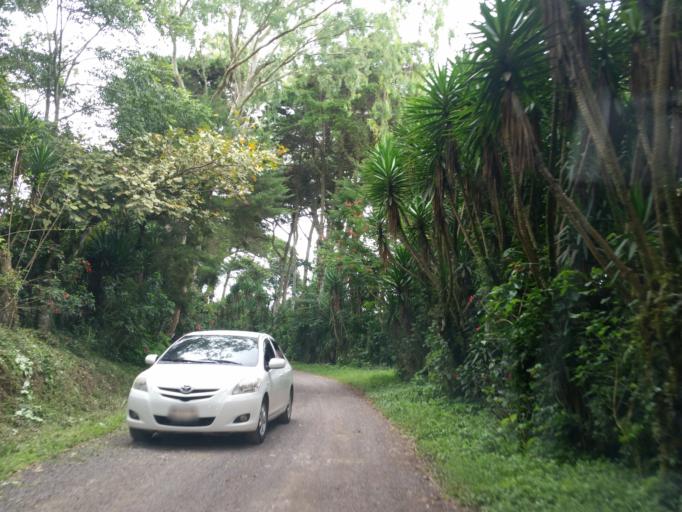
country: NI
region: Matagalpa
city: Matagalpa
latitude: 12.9973
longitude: -85.9178
